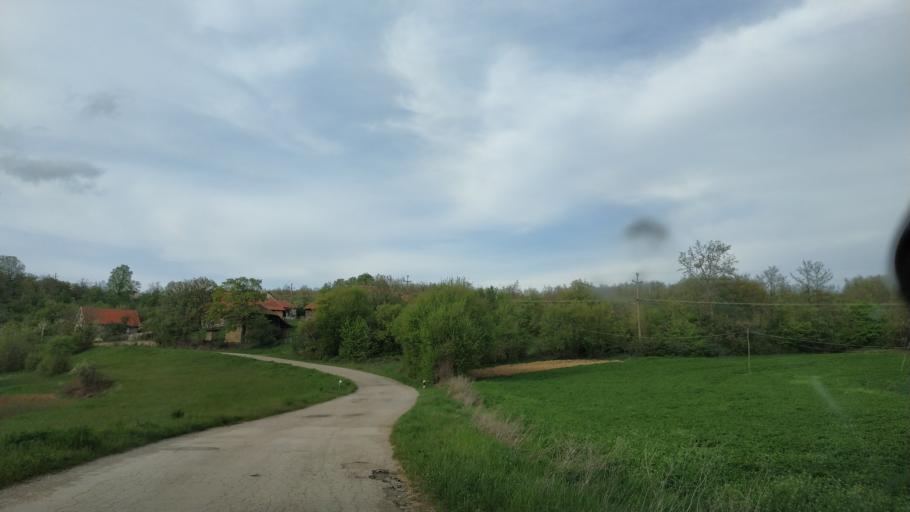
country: RS
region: Central Serbia
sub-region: Zajecarski Okrug
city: Soko Banja
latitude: 43.5373
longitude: 21.8790
